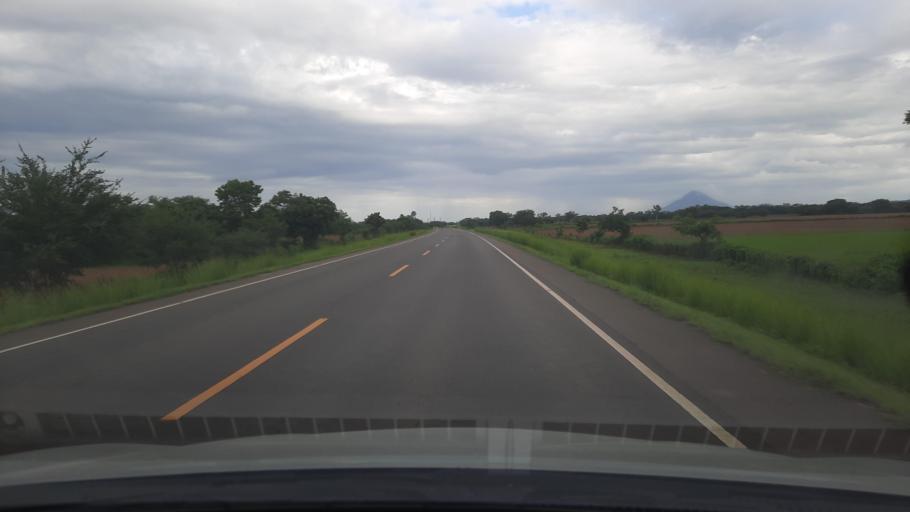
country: NI
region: Leon
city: Larreynaga
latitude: 12.6144
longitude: -86.6834
